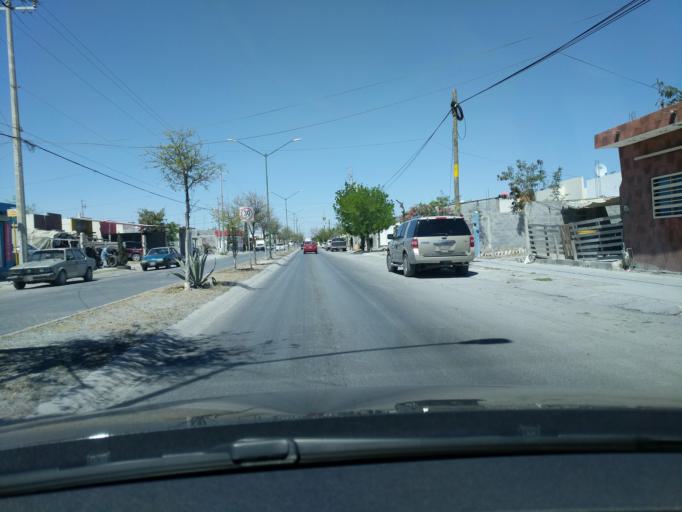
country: MX
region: Nuevo Leon
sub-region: Pesqueria
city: Colinas del Aeropuerto
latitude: 25.8228
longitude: -100.1102
